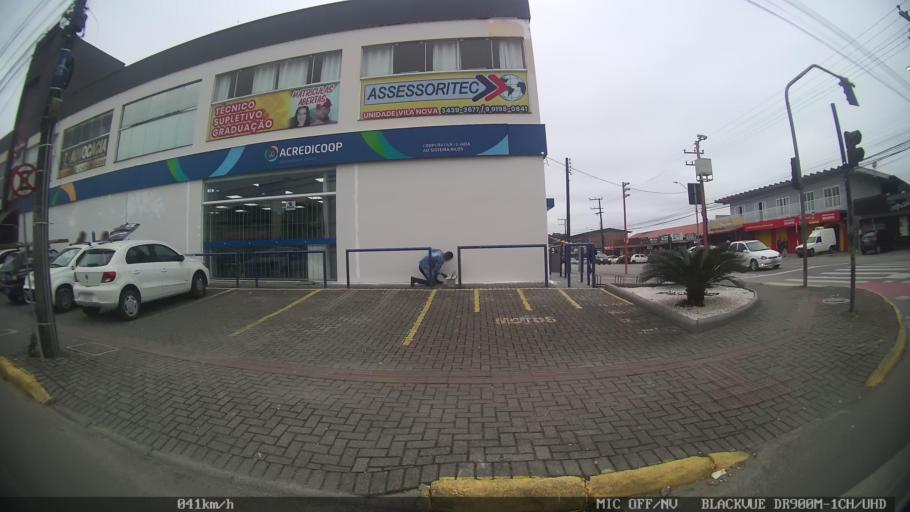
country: BR
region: Santa Catarina
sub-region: Joinville
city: Joinville
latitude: -26.2872
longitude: -48.9023
